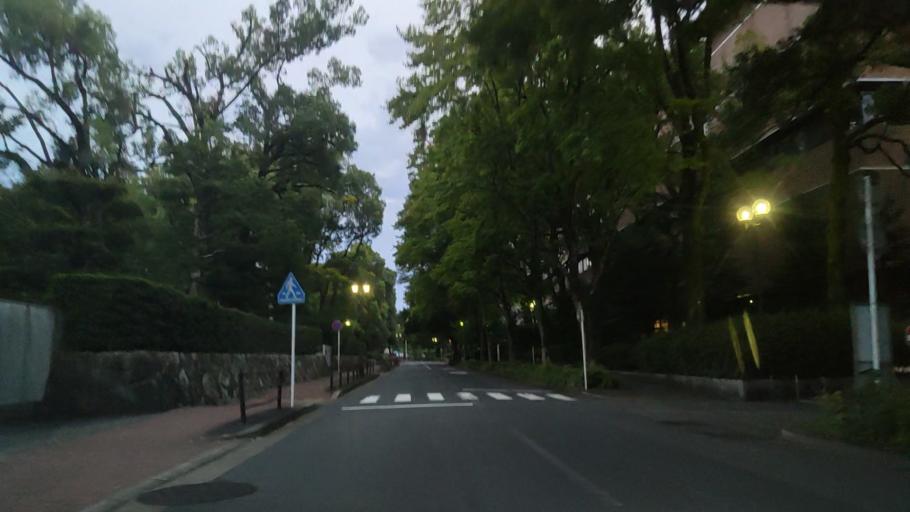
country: JP
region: Aichi
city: Nagoya-shi
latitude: 35.1810
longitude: 136.9077
